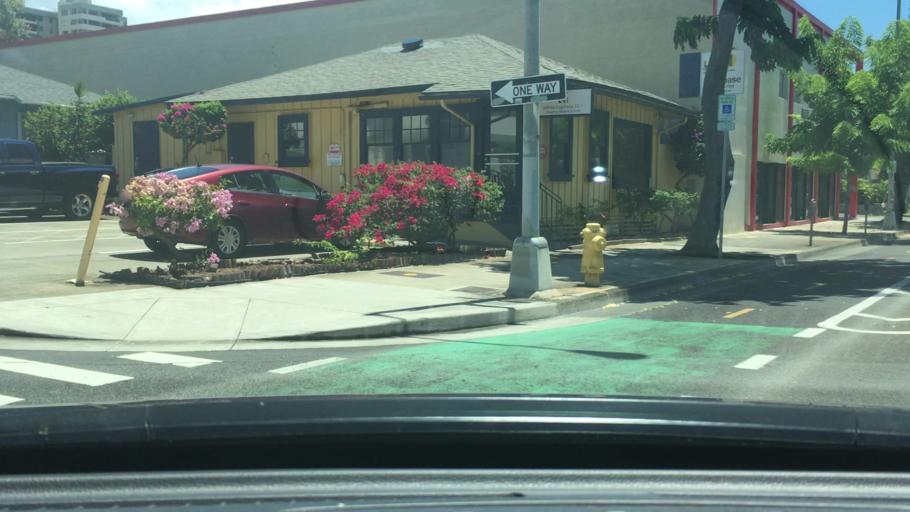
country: US
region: Hawaii
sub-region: Honolulu County
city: Honolulu
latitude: 21.2965
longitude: -157.8345
